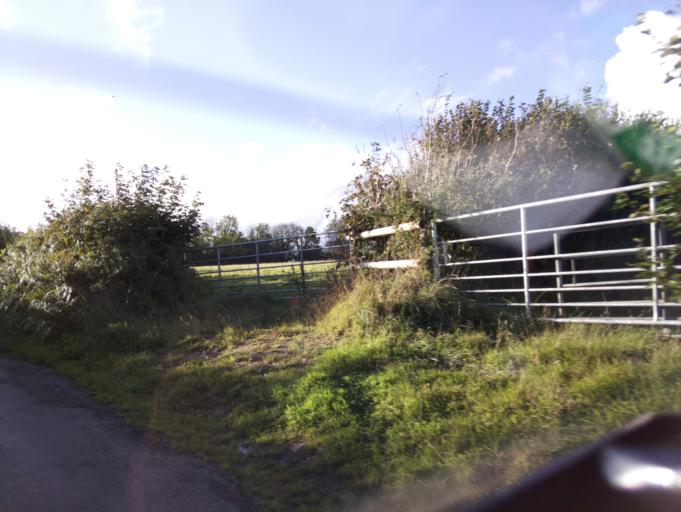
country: GB
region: England
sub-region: Devon
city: Totnes
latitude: 50.3448
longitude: -3.6955
